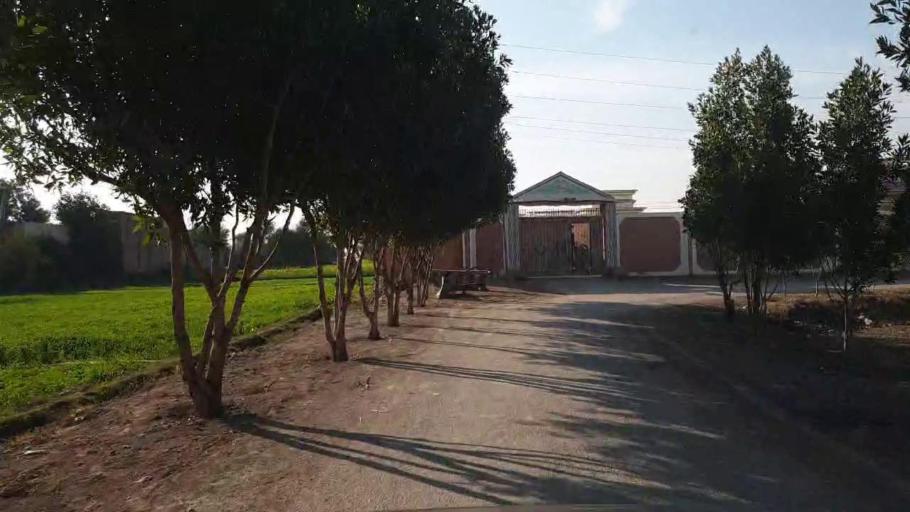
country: PK
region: Sindh
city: Shahpur Chakar
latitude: 26.1573
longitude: 68.6625
